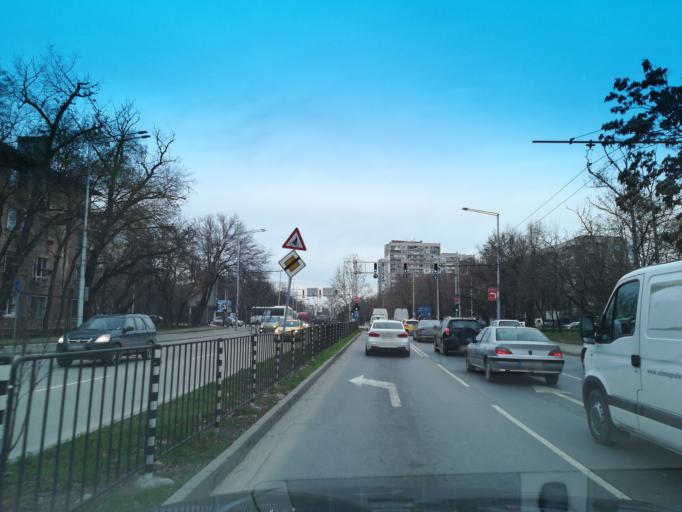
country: BG
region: Plovdiv
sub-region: Obshtina Plovdiv
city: Plovdiv
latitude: 42.1573
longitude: 24.7310
